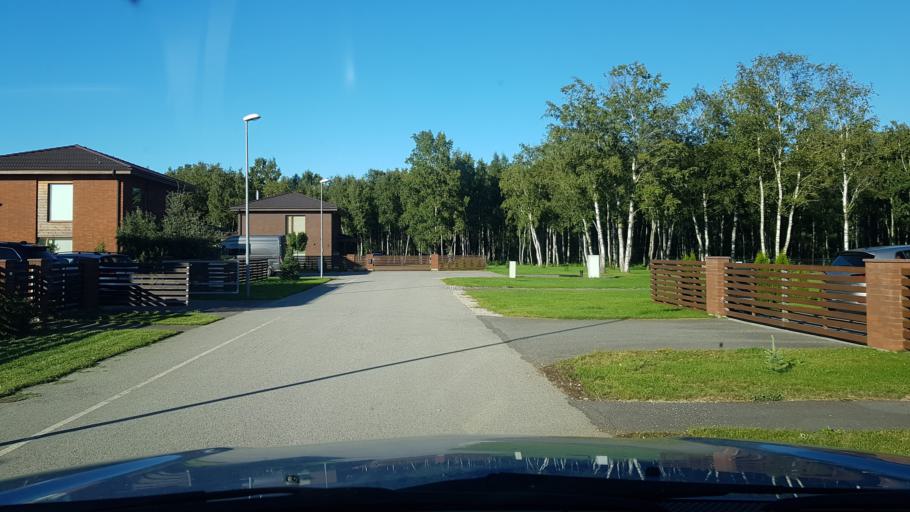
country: EE
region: Harju
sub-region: Rae vald
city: Jueri
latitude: 59.3900
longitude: 24.8562
